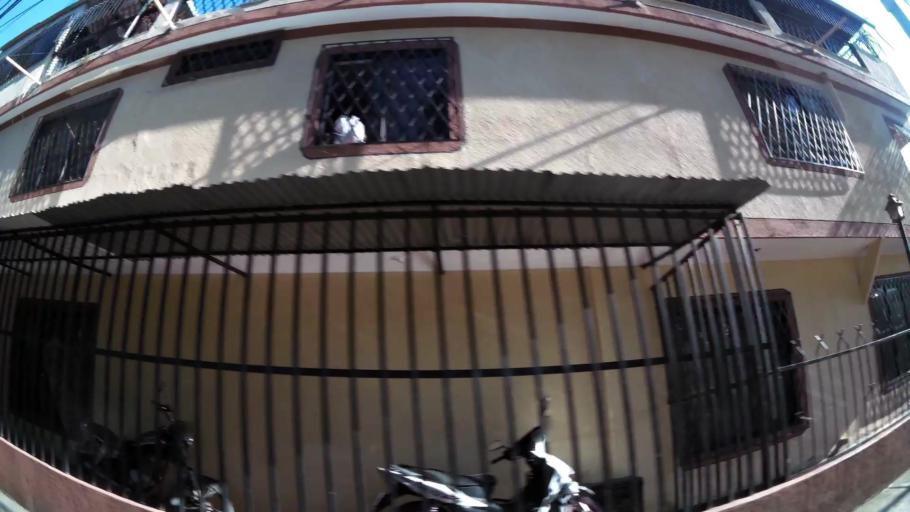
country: CO
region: Valle del Cauca
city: Cali
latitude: 3.4274
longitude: -76.5129
